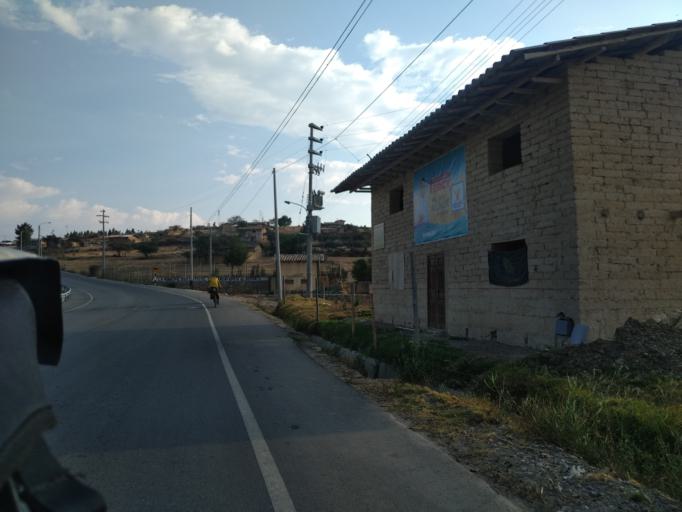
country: PE
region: Cajamarca
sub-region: San Marcos
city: La Grama
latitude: -7.3976
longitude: -78.1254
